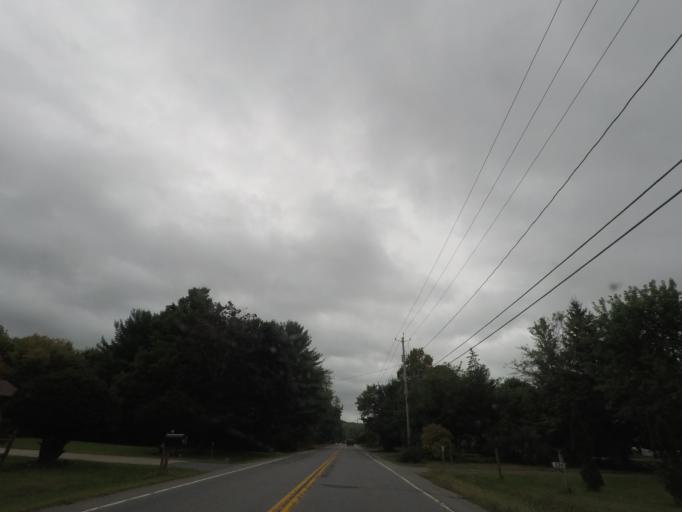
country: US
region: New York
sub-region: Saratoga County
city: Country Knolls
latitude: 42.9444
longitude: -73.7791
